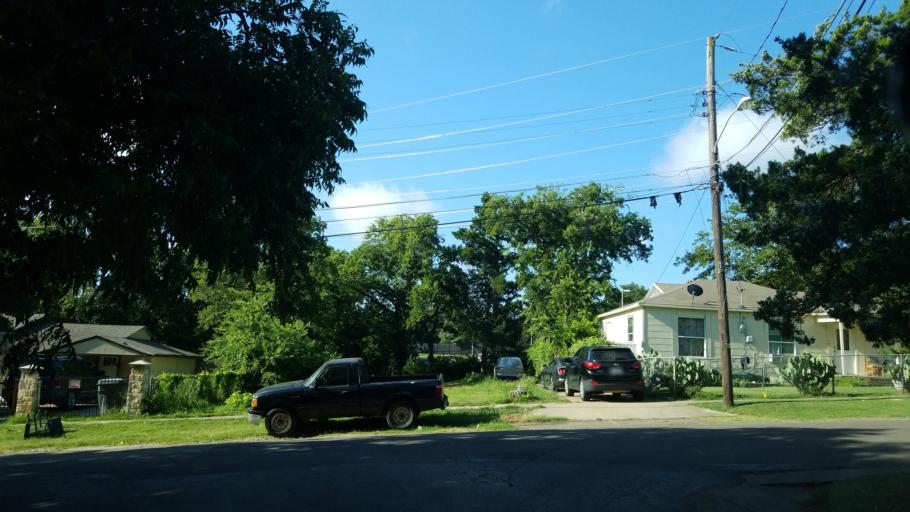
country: US
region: Texas
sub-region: Dallas County
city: Dallas
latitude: 32.7238
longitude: -96.8035
